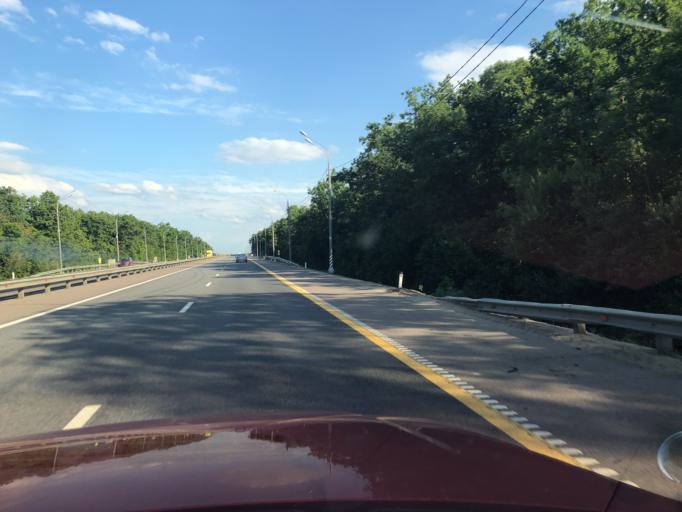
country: RU
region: Lipetsk
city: Zadonsk
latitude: 52.4176
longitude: 38.8401
